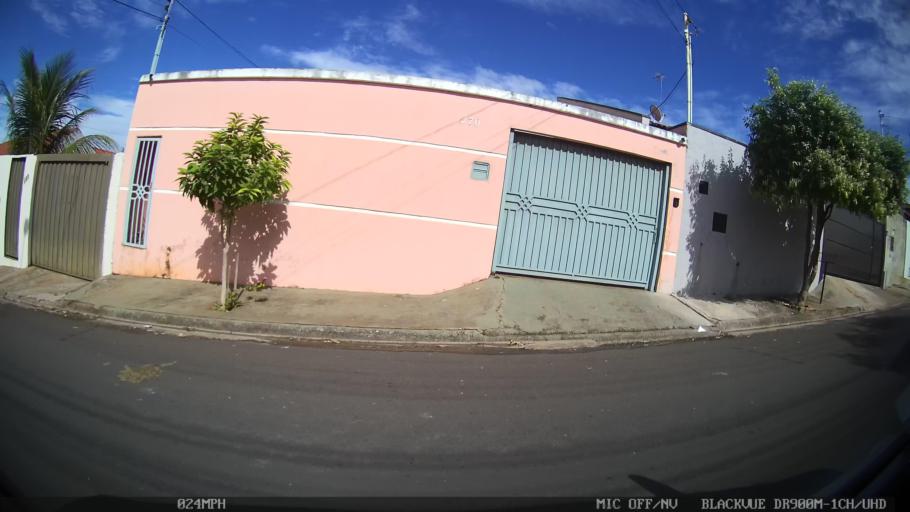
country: BR
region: Sao Paulo
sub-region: Catanduva
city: Catanduva
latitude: -21.1256
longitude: -48.9453
